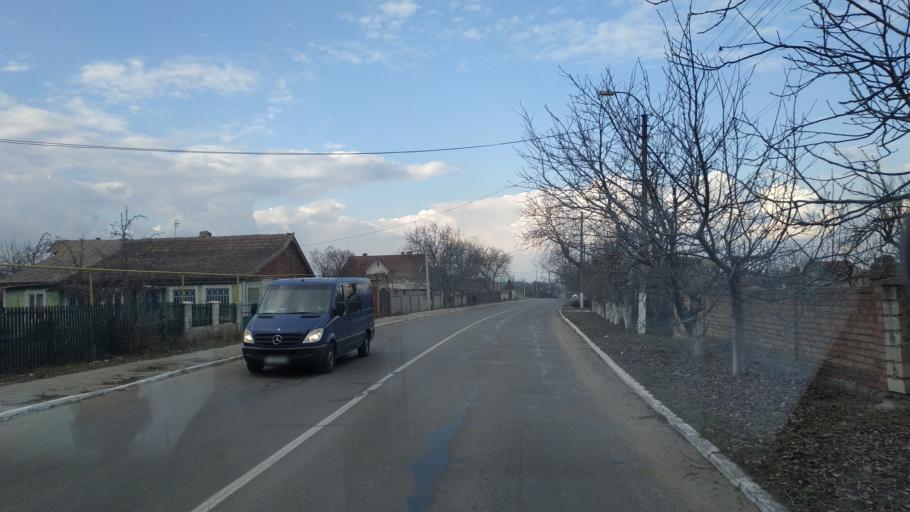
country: MD
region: Anenii Noi
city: Varnita
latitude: 46.8561
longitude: 29.4795
